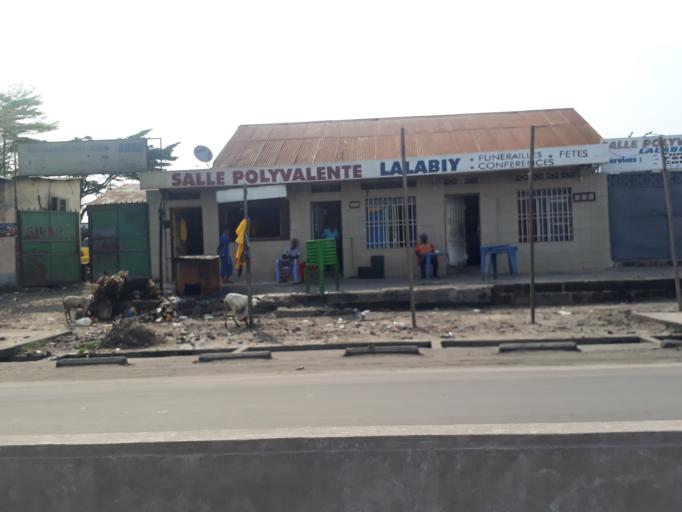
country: CD
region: Kinshasa
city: Kinshasa
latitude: -4.3361
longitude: 15.3057
